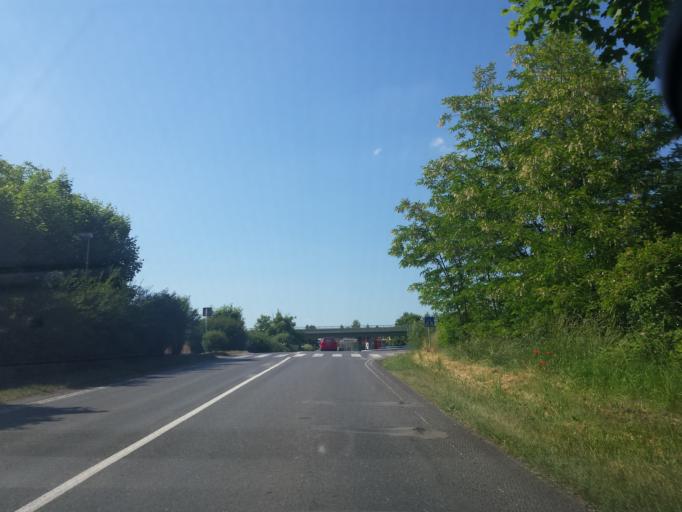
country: CZ
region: Central Bohemia
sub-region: Okres Melnik
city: Veltrusy
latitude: 50.3078
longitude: 14.3142
